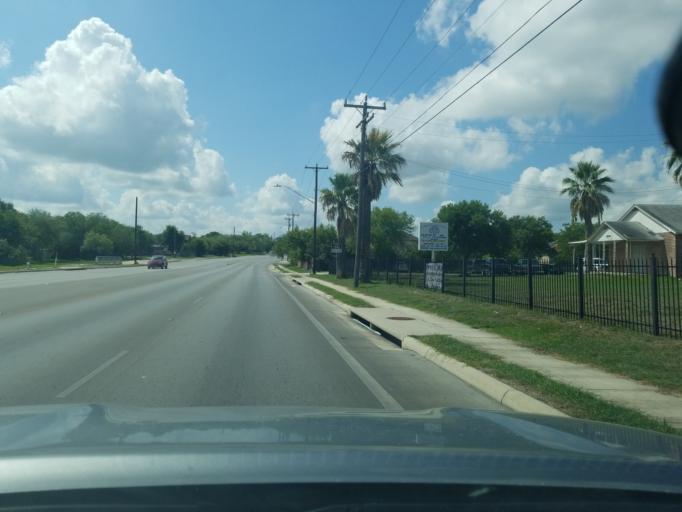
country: US
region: Texas
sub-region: Bexar County
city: Lackland Air Force Base
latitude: 29.3292
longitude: -98.5330
